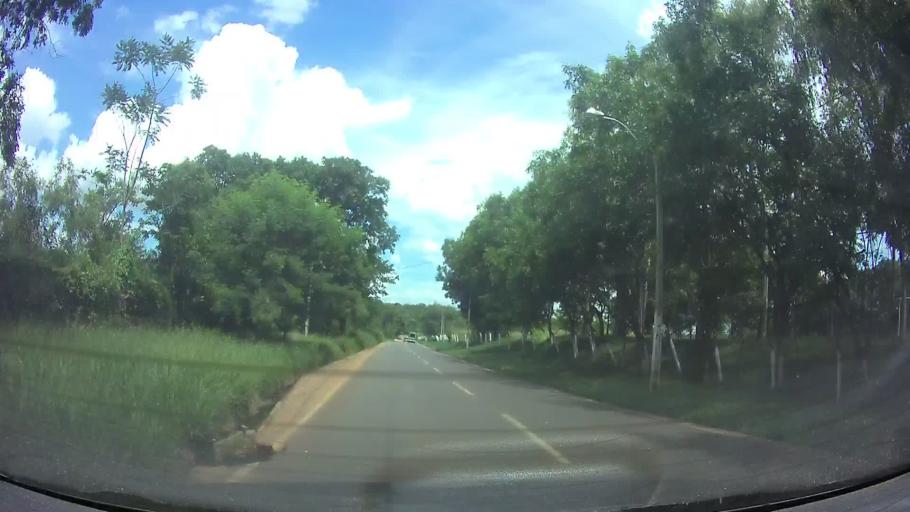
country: PY
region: Central
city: San Lorenzo
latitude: -25.3042
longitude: -57.4943
